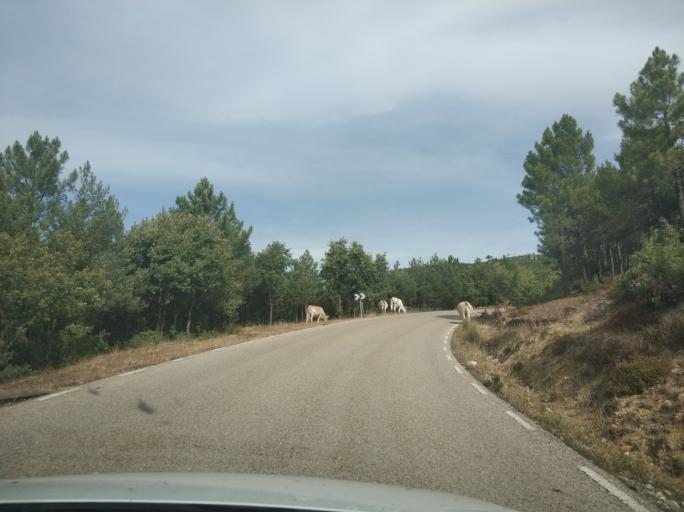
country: ES
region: Castille and Leon
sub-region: Provincia de Soria
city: Duruelo de la Sierra
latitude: 41.9021
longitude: -2.9416
